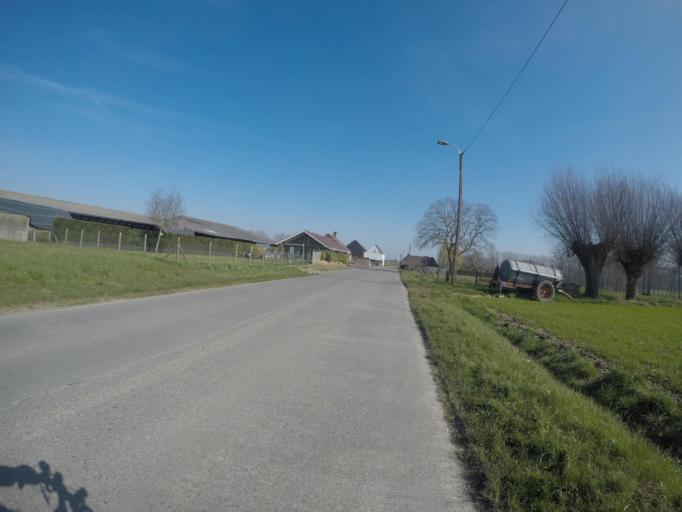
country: BE
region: Flanders
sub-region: Provincie Oost-Vlaanderen
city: Geraardsbergen
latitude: 50.7887
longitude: 3.8588
